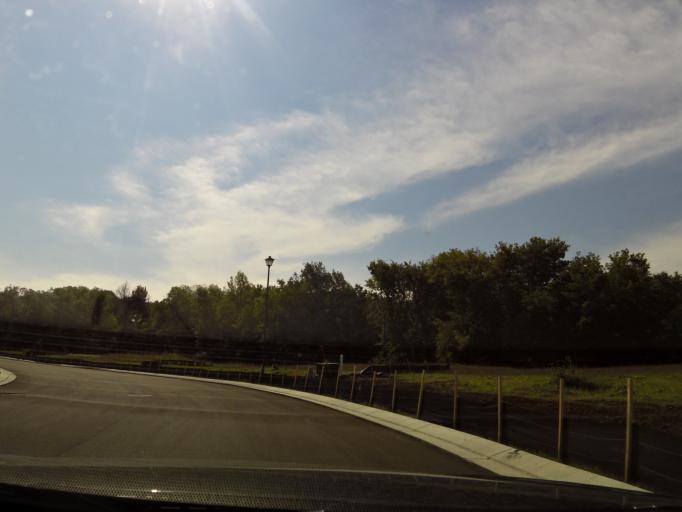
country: US
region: Minnesota
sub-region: Scott County
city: Prior Lake
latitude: 44.7623
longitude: -93.4186
